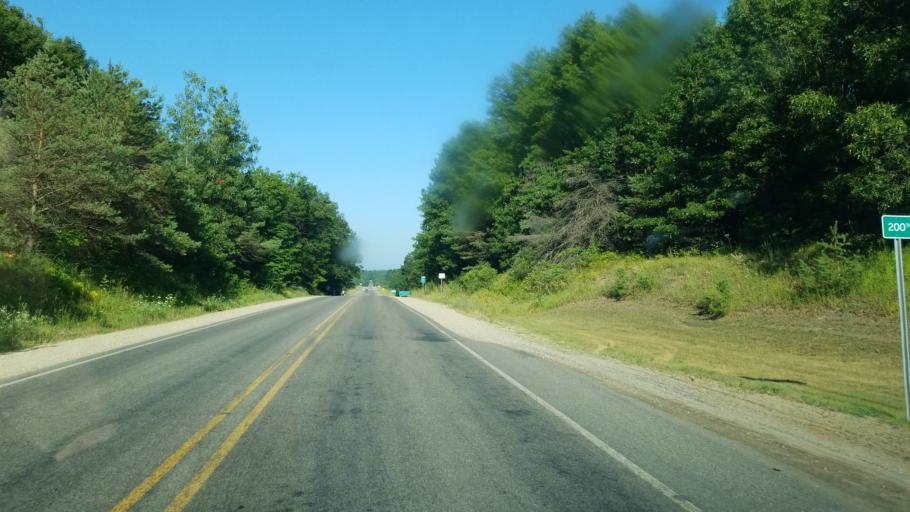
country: US
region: Michigan
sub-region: Montcalm County
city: Howard City
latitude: 43.4898
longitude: -85.4760
